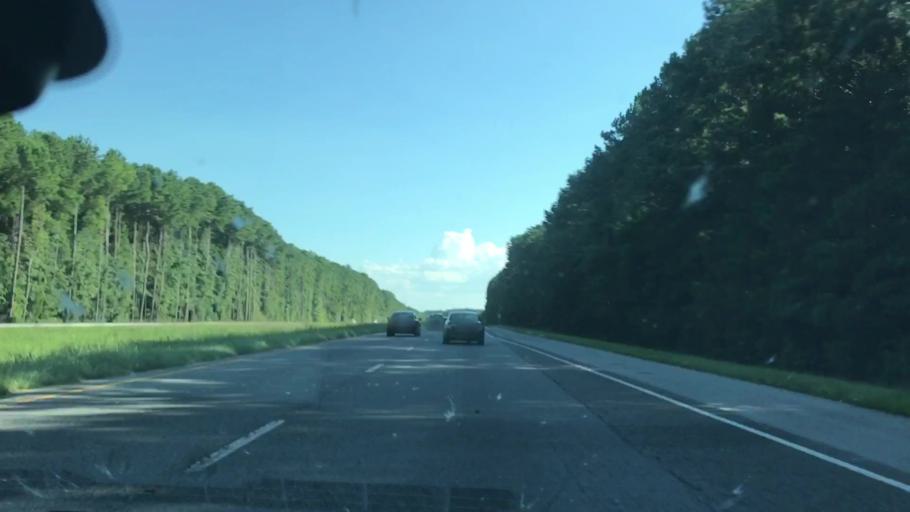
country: US
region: Georgia
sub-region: Harris County
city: Hamilton
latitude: 32.8076
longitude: -85.0214
